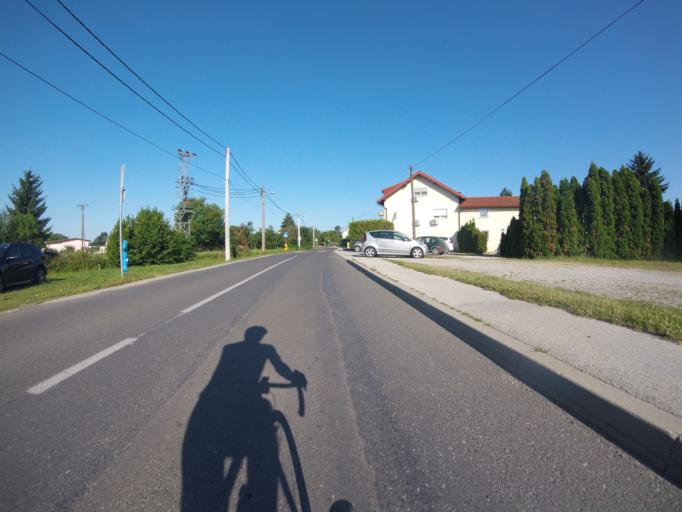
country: HR
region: Grad Zagreb
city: Zadvorsko
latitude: 45.7262
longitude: 15.9172
